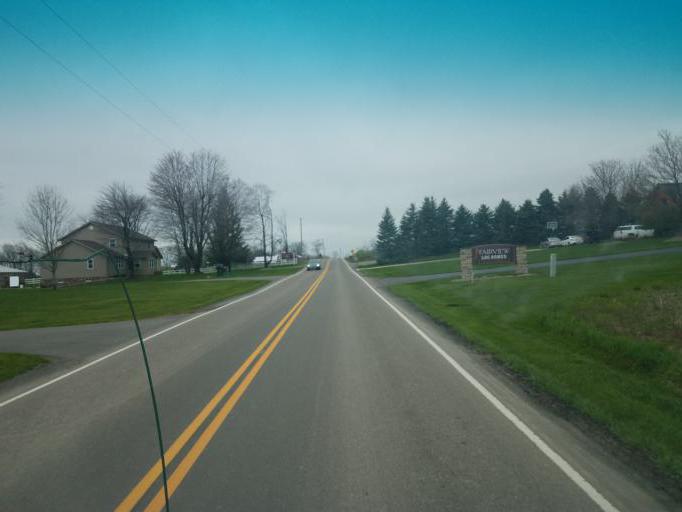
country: US
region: Ohio
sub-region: Tuscarawas County
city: Sugarcreek
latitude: 40.6187
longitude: -81.7394
